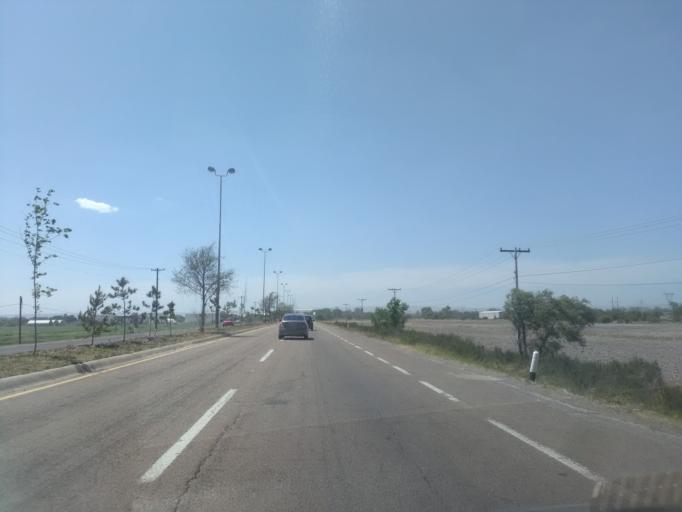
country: MX
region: Durango
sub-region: Durango
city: Jose Refugio Salcido
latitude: 24.0235
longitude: -104.5470
